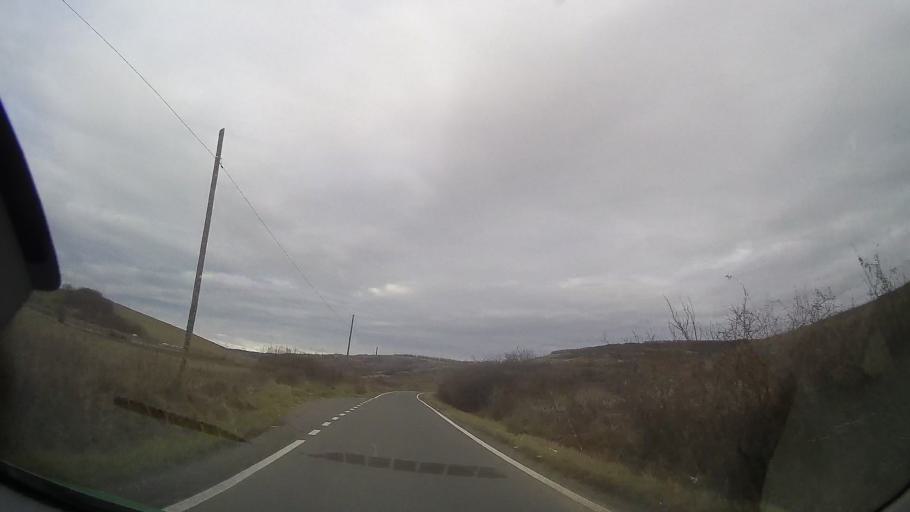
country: RO
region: Mures
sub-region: Comuna Cozma
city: Cozma
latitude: 46.7918
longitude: 24.5431
